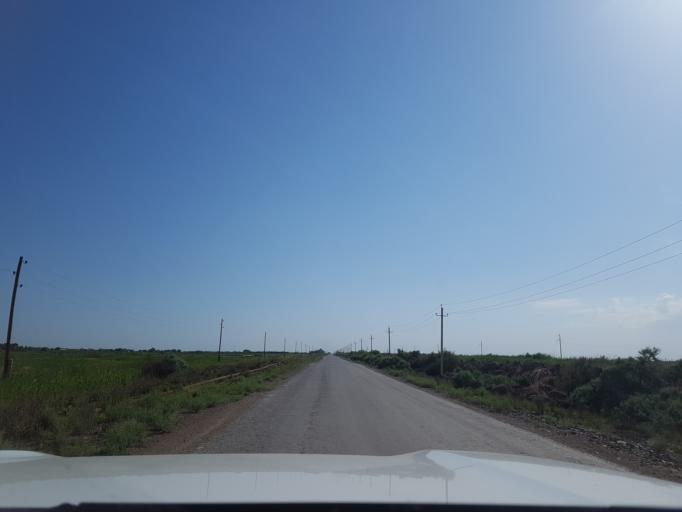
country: TM
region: Dasoguz
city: Koeneuergench
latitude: 42.0892
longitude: 58.8862
